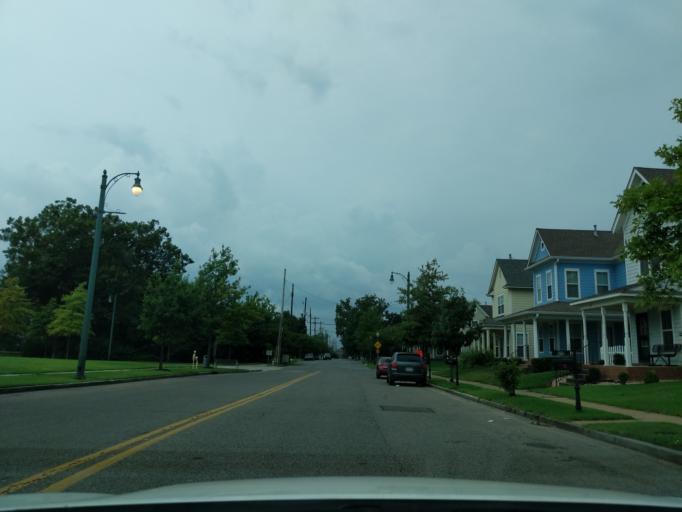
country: US
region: Tennessee
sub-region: Shelby County
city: Memphis
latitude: 35.1569
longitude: -90.0391
